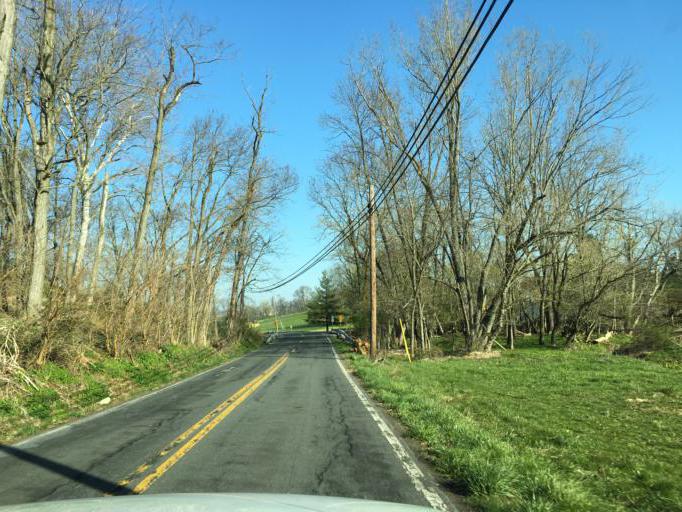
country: US
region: Maryland
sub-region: Frederick County
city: Walkersville
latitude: 39.4917
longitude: -77.3171
